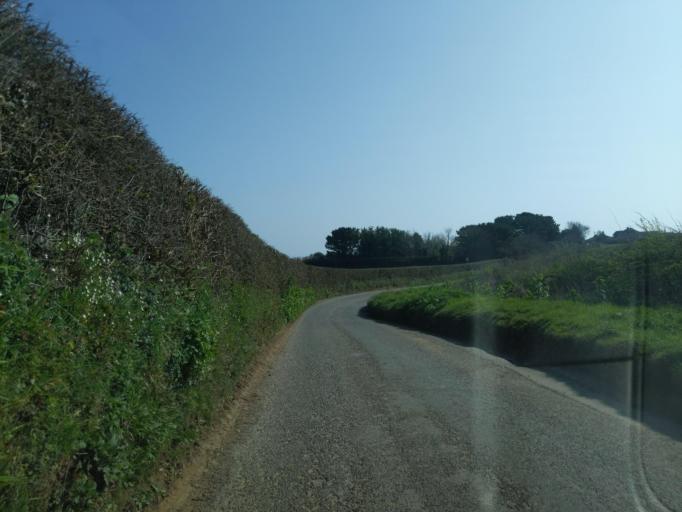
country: GB
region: England
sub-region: Devon
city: Dartmouth
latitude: 50.3165
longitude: -3.6329
